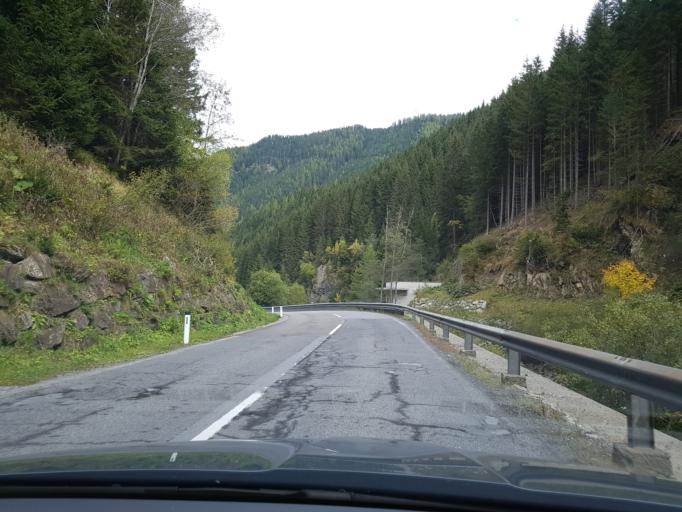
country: AT
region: Salzburg
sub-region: Politischer Bezirk Tamsweg
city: Ramingstein
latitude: 46.9865
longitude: 13.9053
